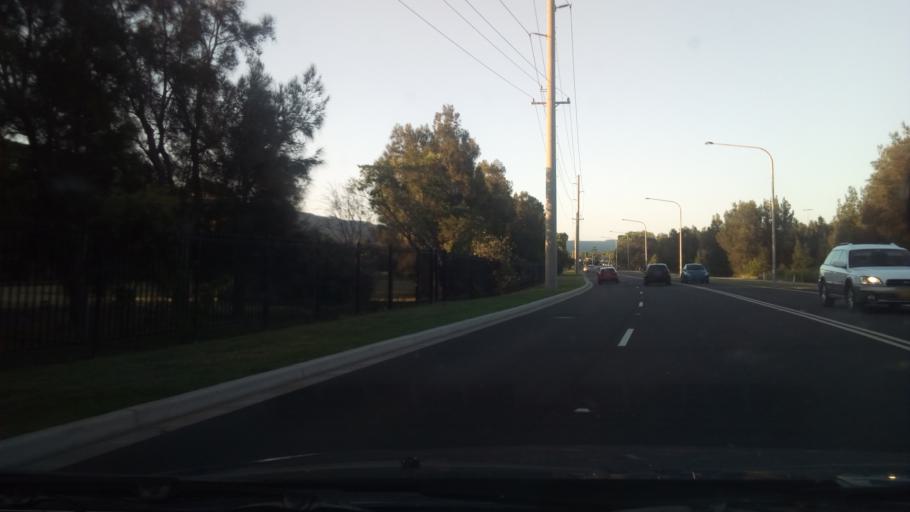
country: AU
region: New South Wales
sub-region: Wollongong
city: Fairy Meadow
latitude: -34.3997
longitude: 150.9008
